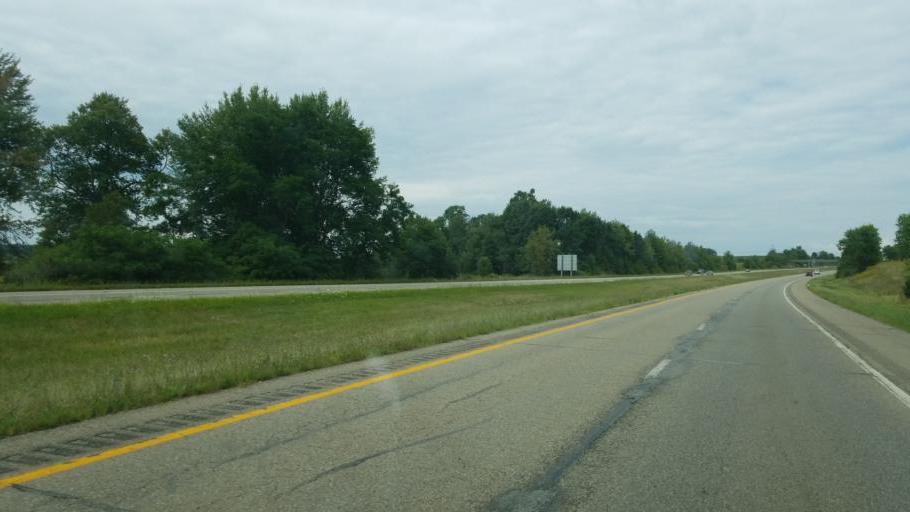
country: US
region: Ohio
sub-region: Columbiana County
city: Columbiana
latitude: 40.8939
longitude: -80.7236
